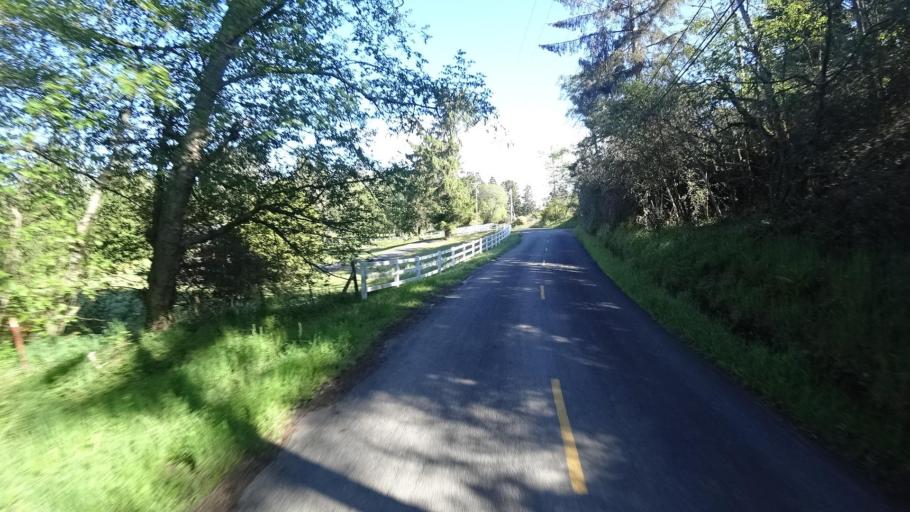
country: US
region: California
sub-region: Humboldt County
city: McKinleyville
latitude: 40.9955
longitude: -124.0994
